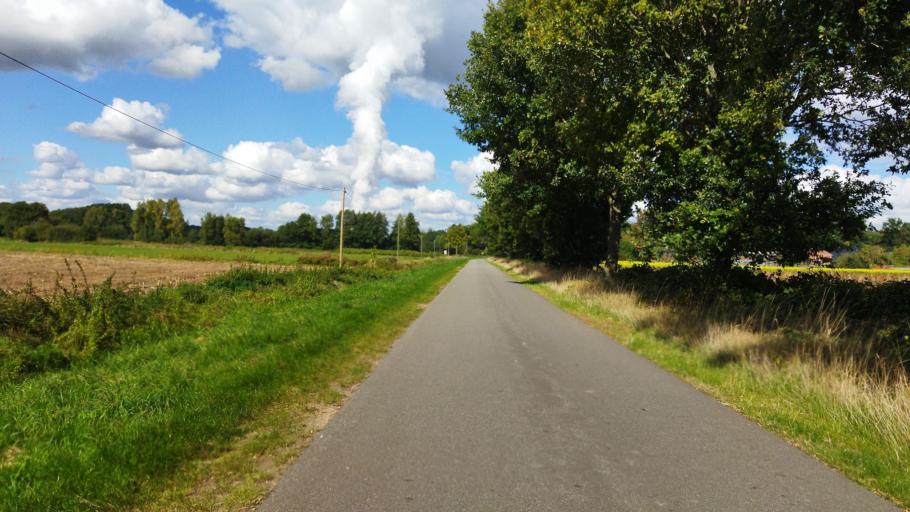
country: DE
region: Lower Saxony
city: Emsburen
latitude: 52.4437
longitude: 7.3385
